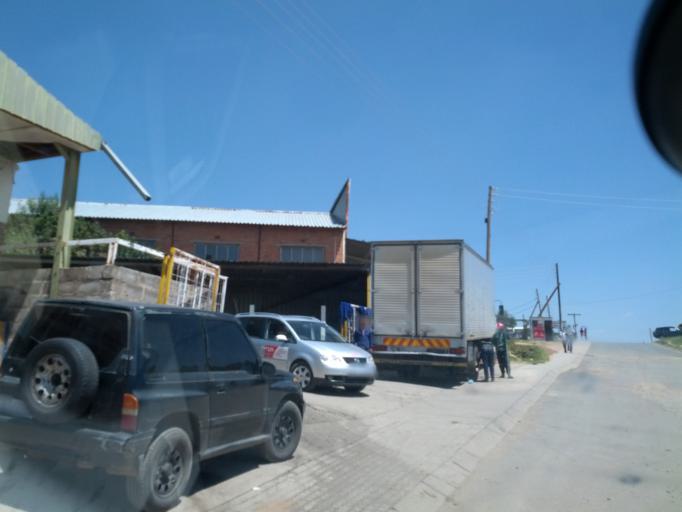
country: LS
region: Butha-Buthe
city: Butha-Buthe
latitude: -28.7675
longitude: 28.2498
